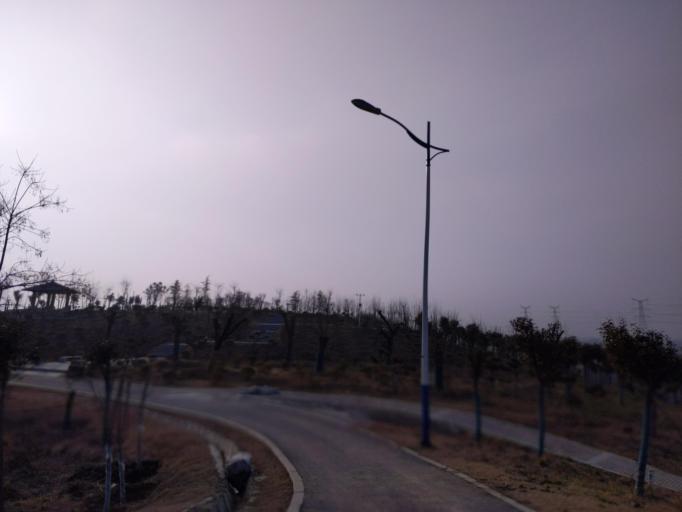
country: CN
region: Henan Sheng
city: Puyang
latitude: 35.8201
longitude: 115.0095
